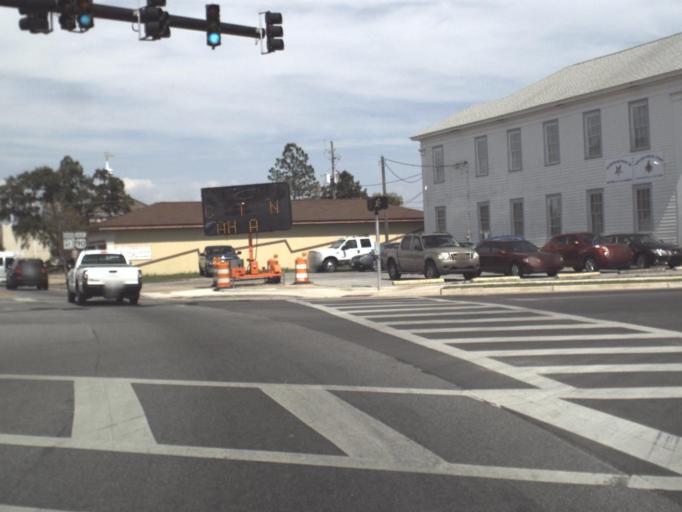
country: US
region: Florida
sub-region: Santa Rosa County
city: Milton
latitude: 30.6216
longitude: -87.0393
